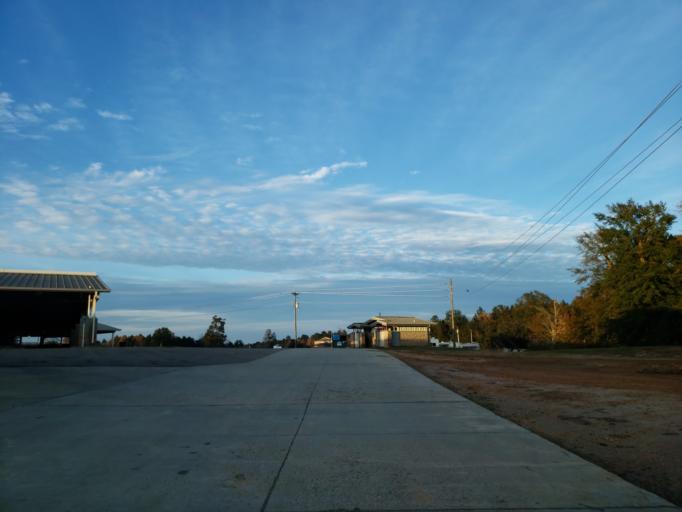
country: US
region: Mississippi
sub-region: Forrest County
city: Hattiesburg
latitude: 31.2574
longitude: -89.2743
